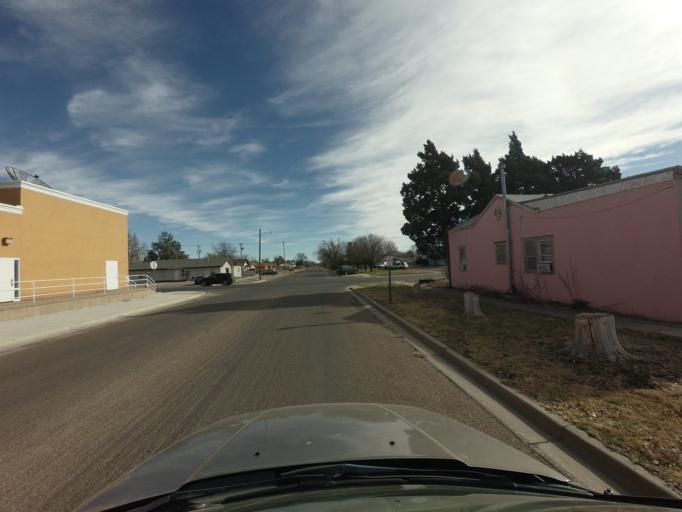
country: US
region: New Mexico
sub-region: Curry County
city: Clovis
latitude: 34.4078
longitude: -103.2045
